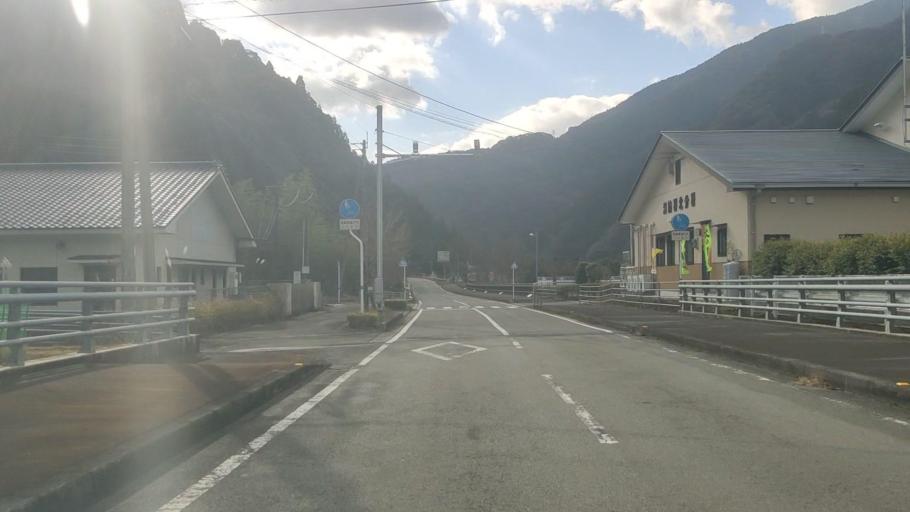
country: JP
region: Kumamoto
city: Hitoyoshi
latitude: 32.3962
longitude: 130.8267
